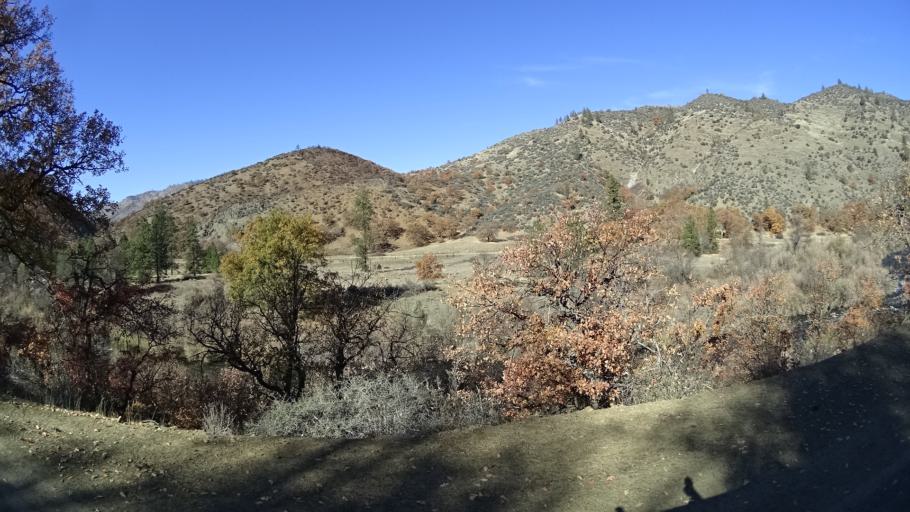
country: US
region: California
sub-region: Siskiyou County
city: Yreka
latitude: 41.8627
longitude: -122.7139
